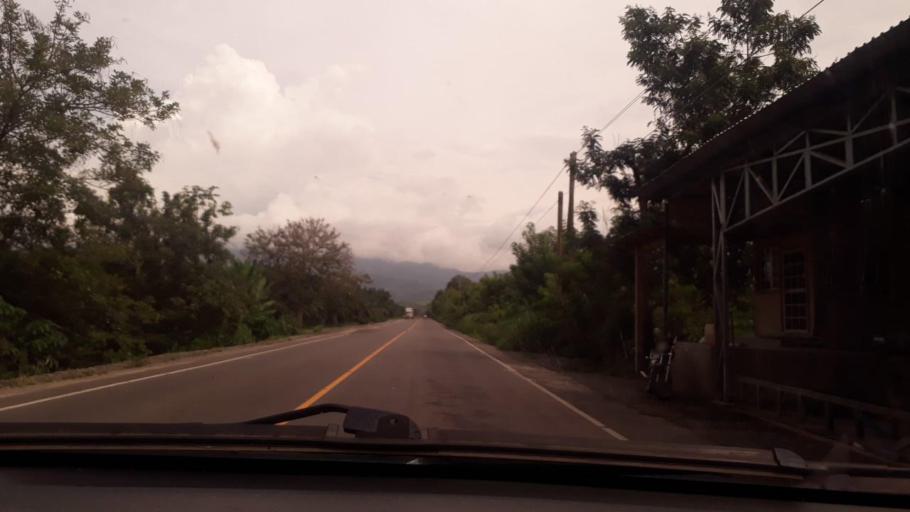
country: HN
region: Cortes
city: Potrerillos
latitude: 15.6178
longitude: -88.3977
